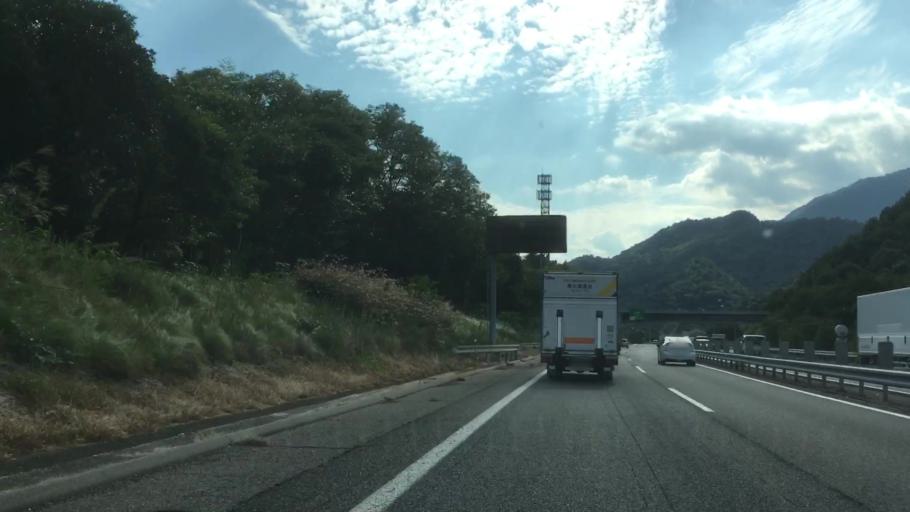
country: JP
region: Hiroshima
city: Ono-hara
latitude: 34.3025
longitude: 132.2765
